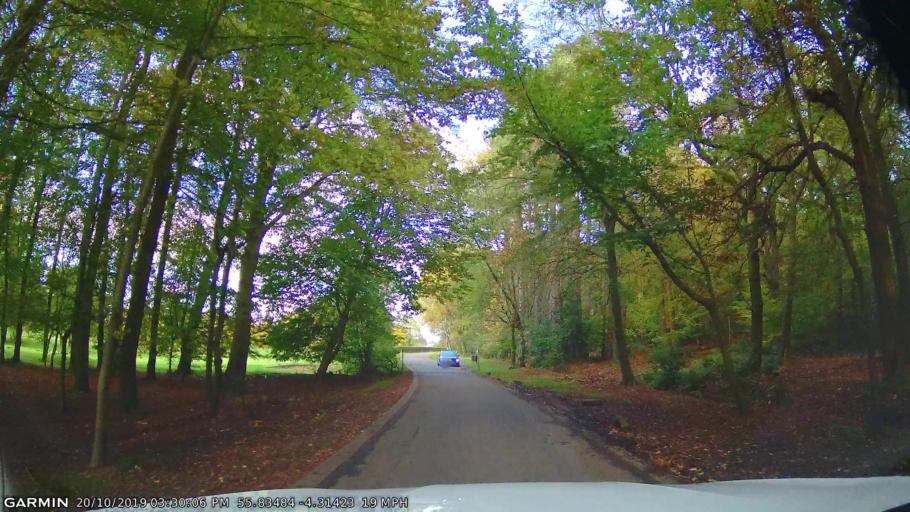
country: GB
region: Scotland
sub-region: East Renfrewshire
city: Giffnock
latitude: 55.8348
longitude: -4.3142
